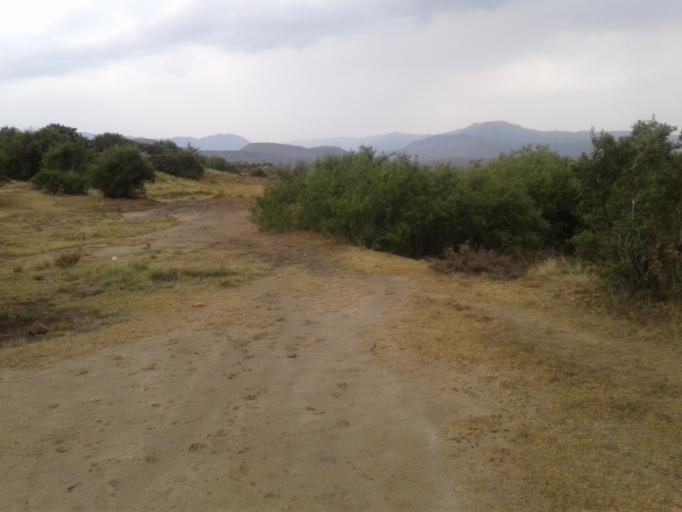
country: LS
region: Quthing
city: Quthing
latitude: -30.3830
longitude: 27.5601
